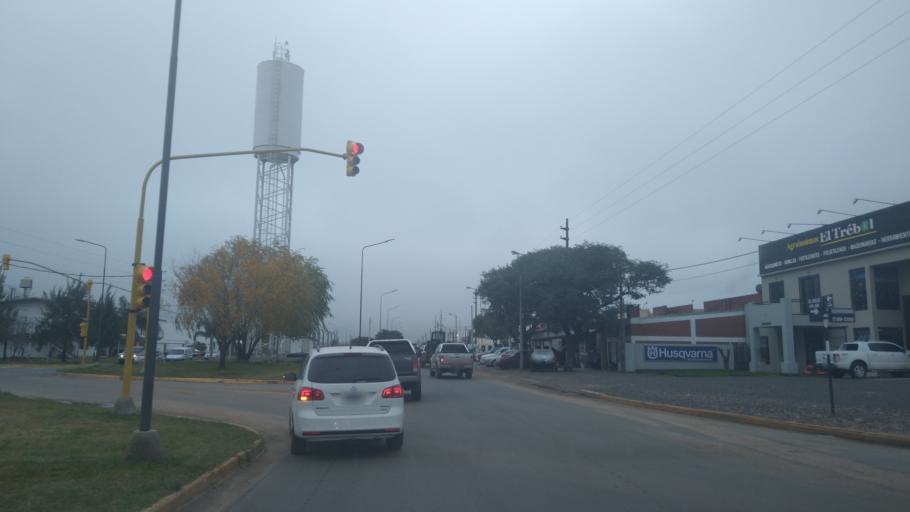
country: AR
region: Entre Rios
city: Chajari
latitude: -30.7607
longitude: -58.0021
